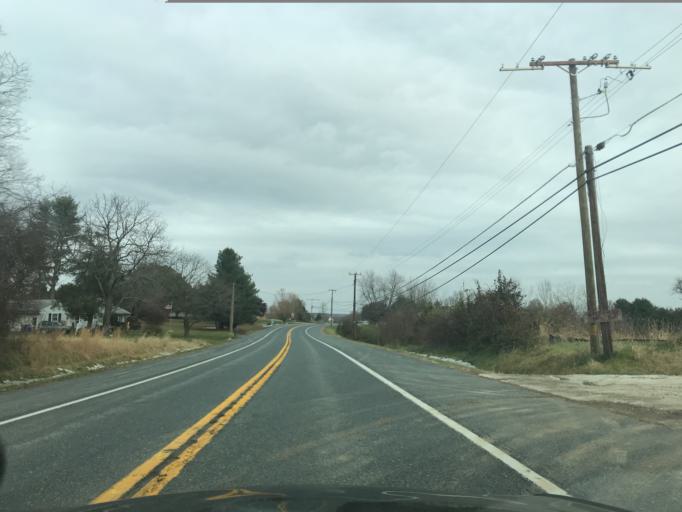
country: US
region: Maryland
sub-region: Harford County
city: Jarrettsville
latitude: 39.6512
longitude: -76.4655
